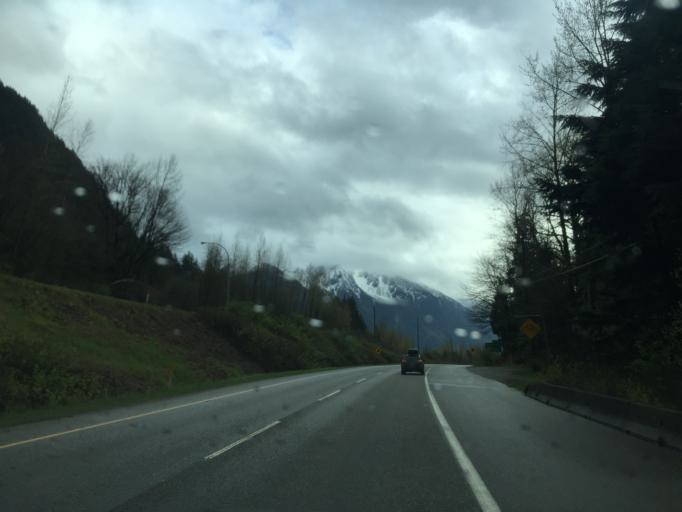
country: CA
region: British Columbia
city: Agassiz
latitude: 49.2613
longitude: -121.6762
